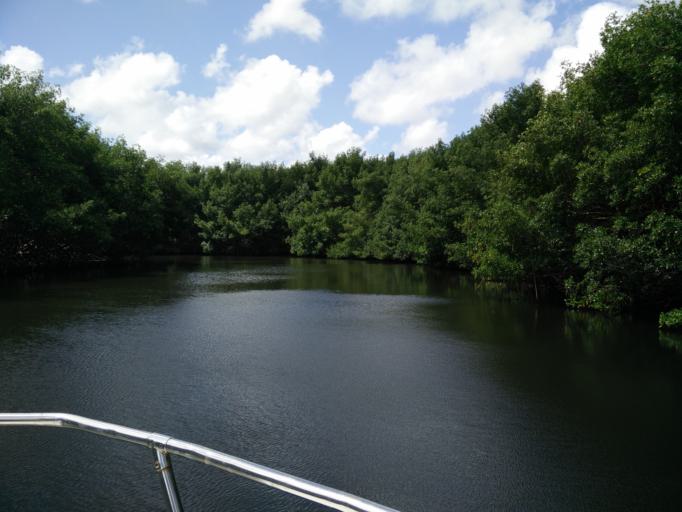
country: GP
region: Guadeloupe
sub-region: Guadeloupe
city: Petit-Canal
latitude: 16.3536
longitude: -61.4912
